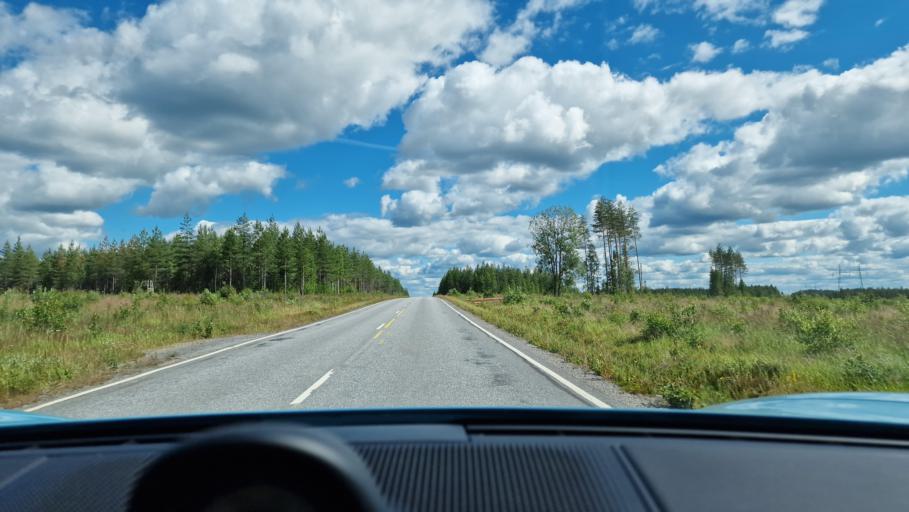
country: FI
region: Central Finland
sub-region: Saarijaervi-Viitasaari
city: Pylkoenmaeki
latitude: 62.6624
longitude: 24.5554
